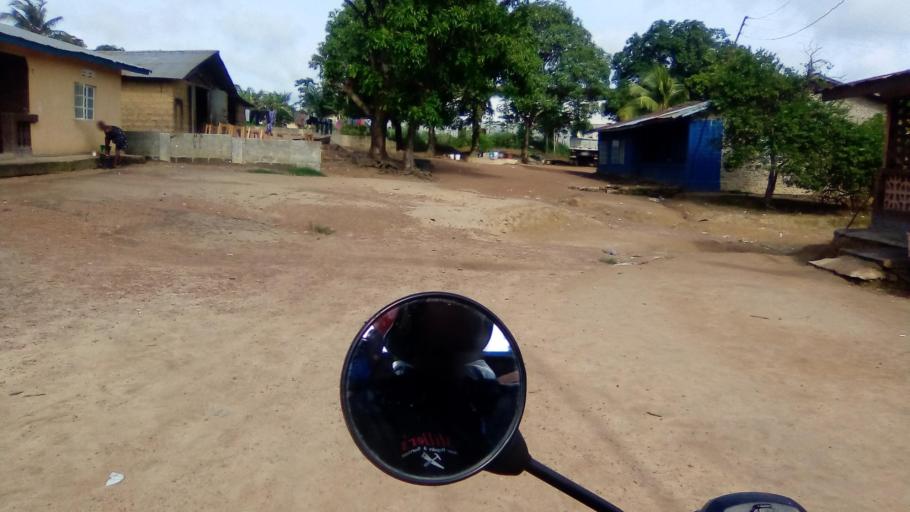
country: SL
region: Southern Province
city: Bo
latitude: 7.9568
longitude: -11.7589
